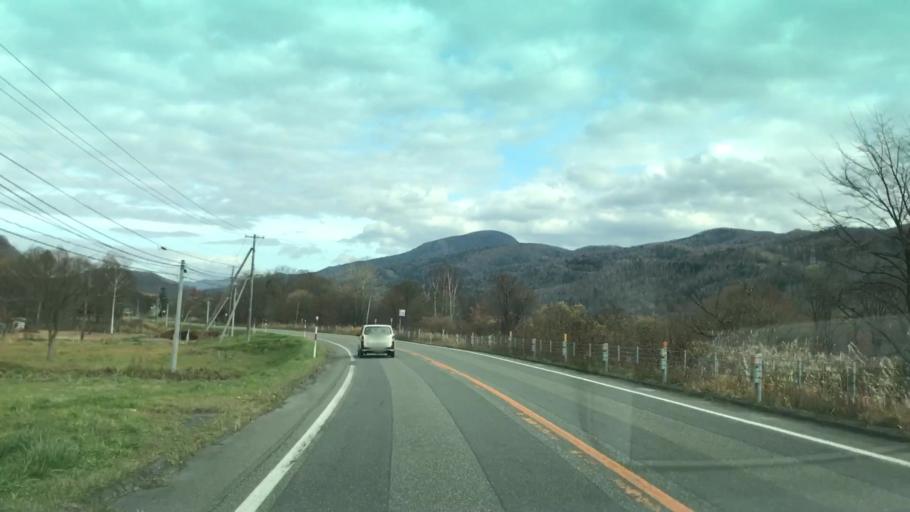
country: JP
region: Hokkaido
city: Shizunai-furukawacho
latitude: 42.7693
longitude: 142.3791
